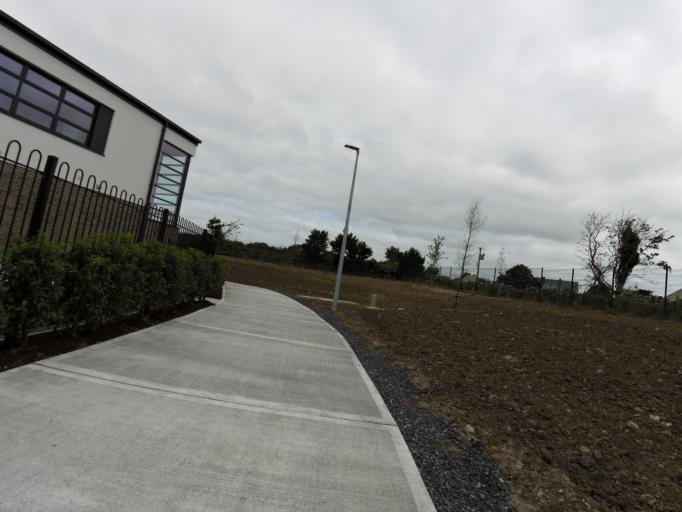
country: IE
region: Connaught
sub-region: County Galway
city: Athenry
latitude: 53.2939
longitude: -8.7546
